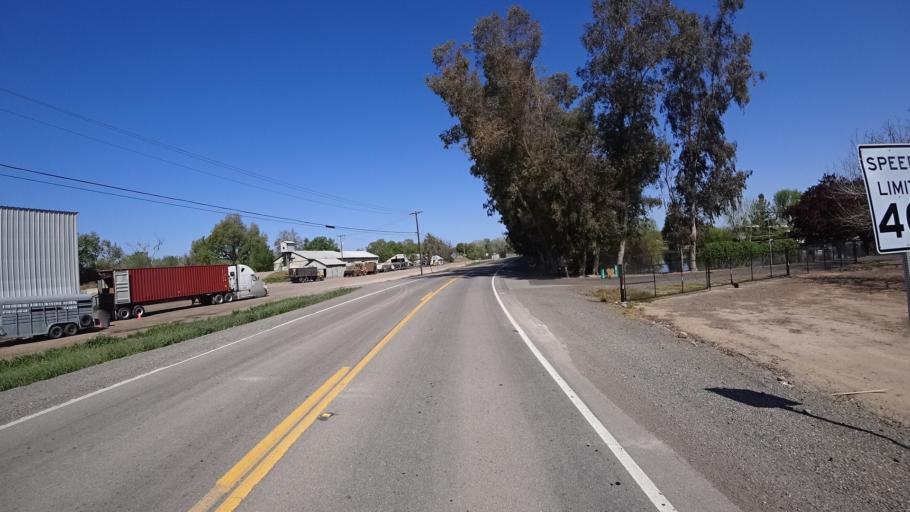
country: US
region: California
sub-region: Glenn County
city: Willows
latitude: 39.4596
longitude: -121.9927
